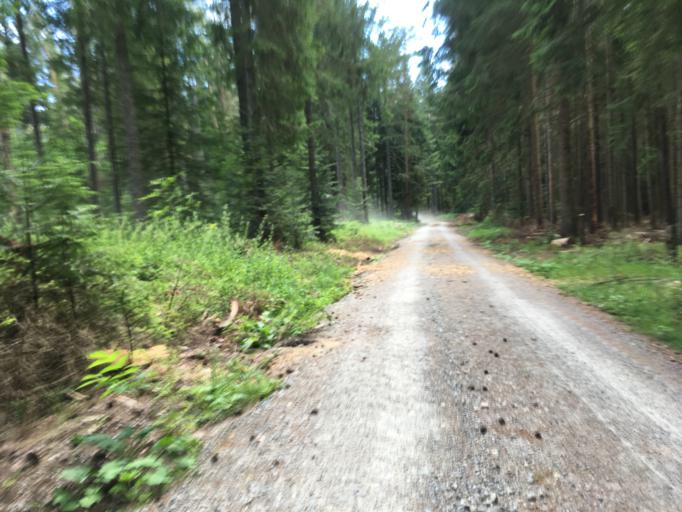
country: DE
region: Baden-Wuerttemberg
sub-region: Karlsruhe Region
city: Baiersbronn
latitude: 48.5520
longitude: 8.4186
